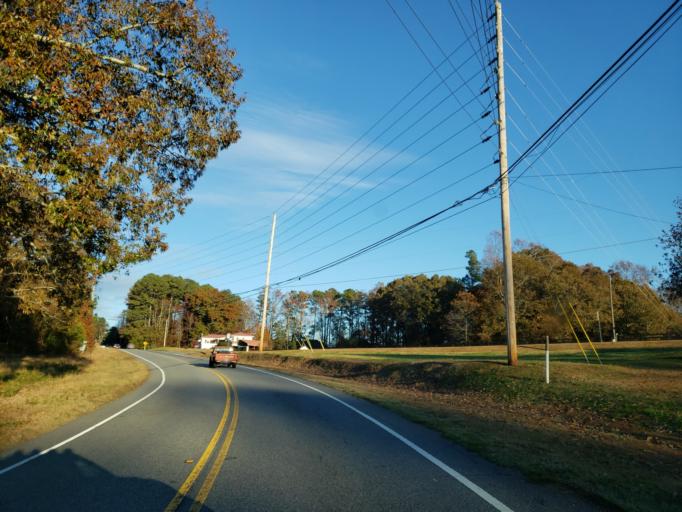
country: US
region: Georgia
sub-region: Cherokee County
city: Canton
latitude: 34.2158
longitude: -84.3851
